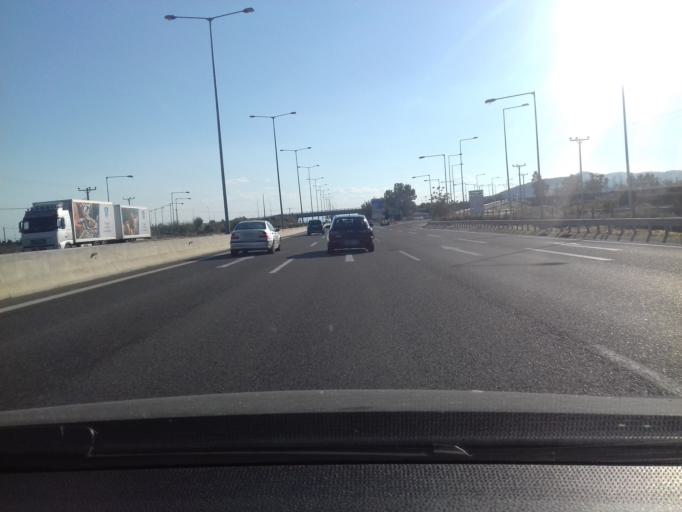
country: GR
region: Attica
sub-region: Nomarchia Dytikis Attikis
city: Megara
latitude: 37.9889
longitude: 23.3551
